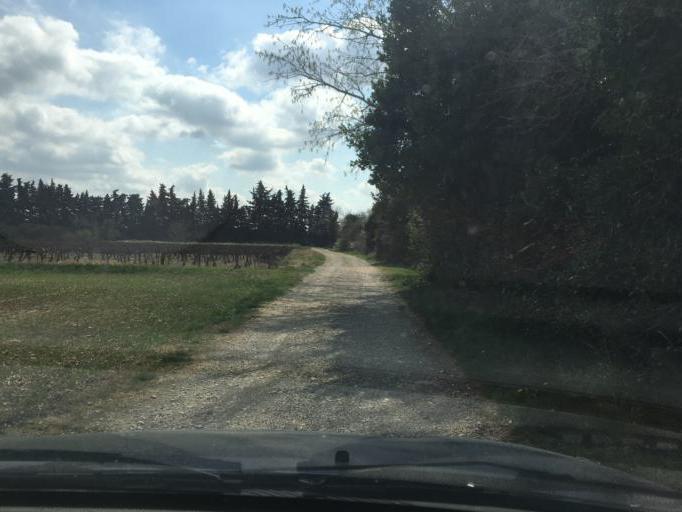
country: FR
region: Provence-Alpes-Cote d'Azur
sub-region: Departement du Vaucluse
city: Serignan-du-Comtat
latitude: 44.1694
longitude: 4.8207
